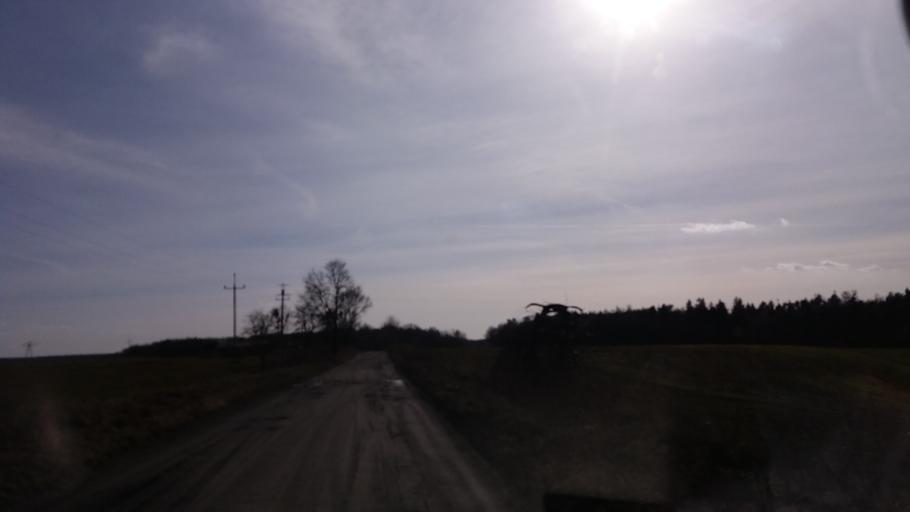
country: PL
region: West Pomeranian Voivodeship
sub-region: Powiat choszczenski
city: Pelczyce
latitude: 53.0094
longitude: 15.3700
